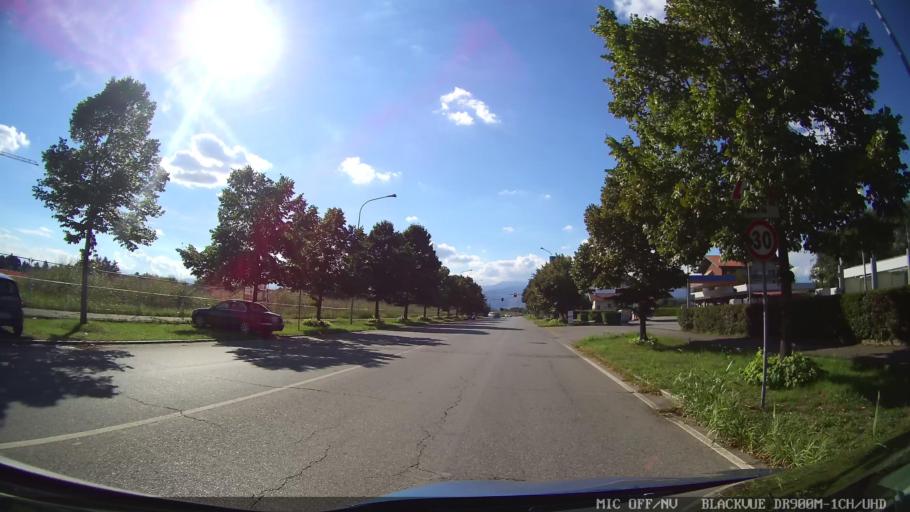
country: IT
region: Piedmont
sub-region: Provincia di Torino
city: Savonera
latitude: 45.1217
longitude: 7.6202
